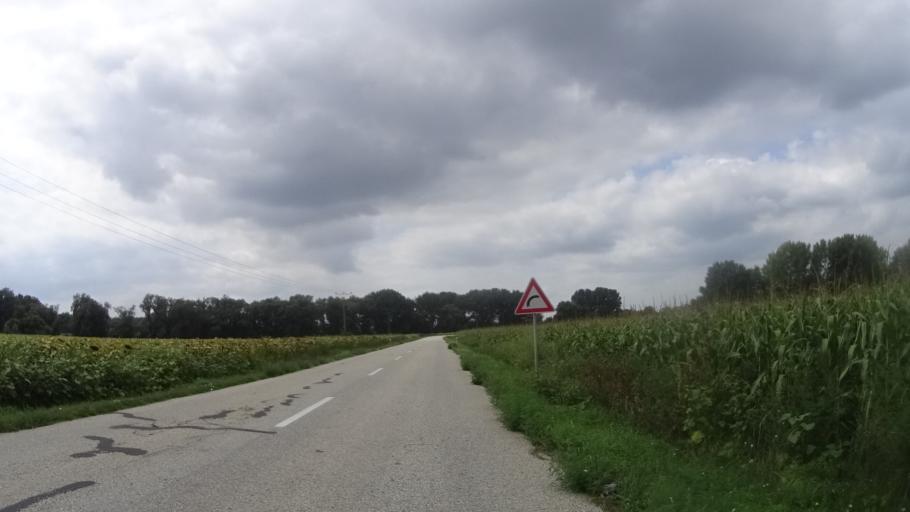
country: HU
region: Gyor-Moson-Sopron
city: Bony
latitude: 47.7514
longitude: 17.8529
